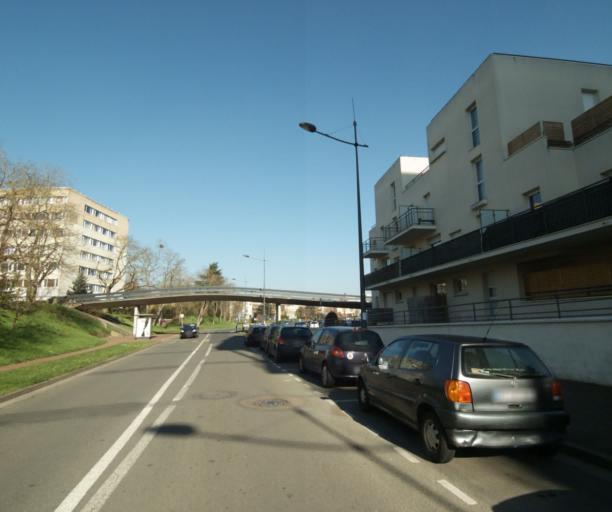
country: FR
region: Ile-de-France
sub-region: Departement du Val-d'Oise
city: Cergy
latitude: 49.0304
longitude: 2.0817
